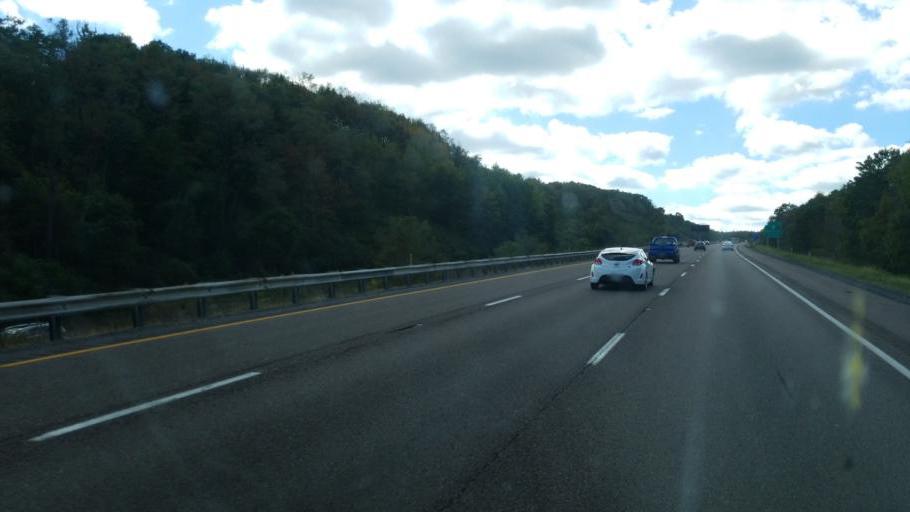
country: US
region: Maryland
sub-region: Allegany County
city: Frostburg
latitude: 39.6365
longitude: -78.9023
